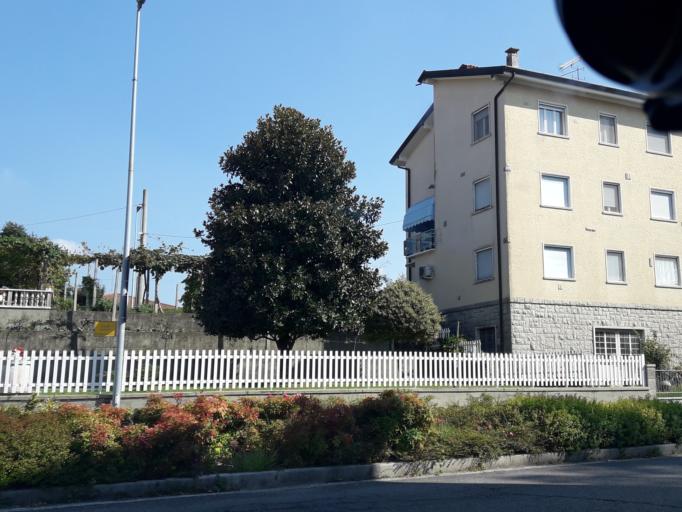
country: IT
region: Friuli Venezia Giulia
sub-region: Provincia di Udine
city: Tavagnacco
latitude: 46.1156
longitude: 13.2104
